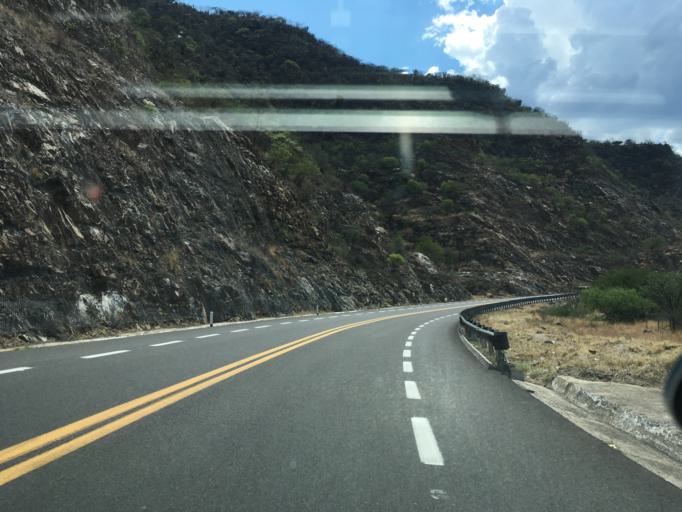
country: MX
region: Puebla
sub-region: San Jose Miahuatlan
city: San Pedro Tetitlan
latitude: 18.1527
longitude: -97.2992
